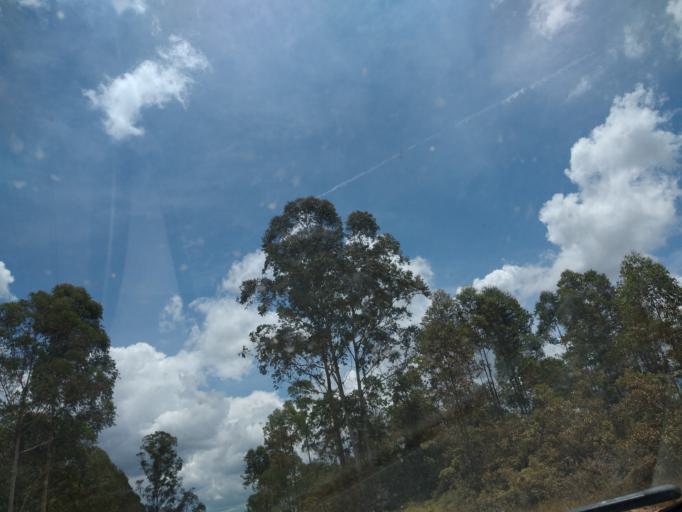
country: BR
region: Minas Gerais
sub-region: Sao Joao Del Rei
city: Sao Joao del Rei
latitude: -20.9059
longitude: -44.2867
